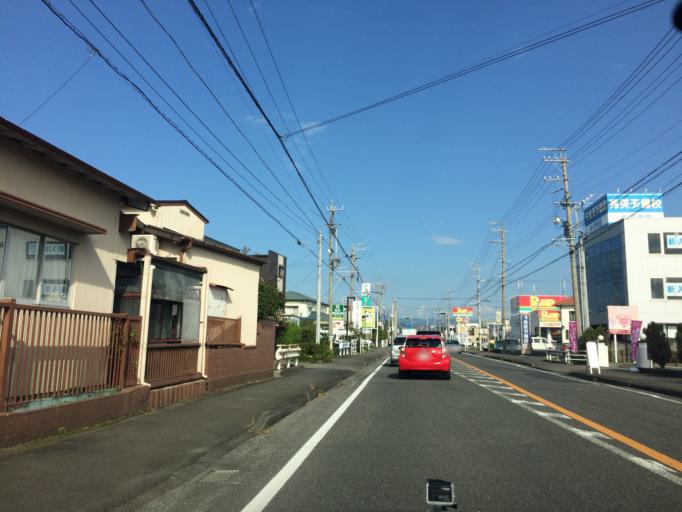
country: JP
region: Shizuoka
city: Fujieda
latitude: 34.8375
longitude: 138.2650
